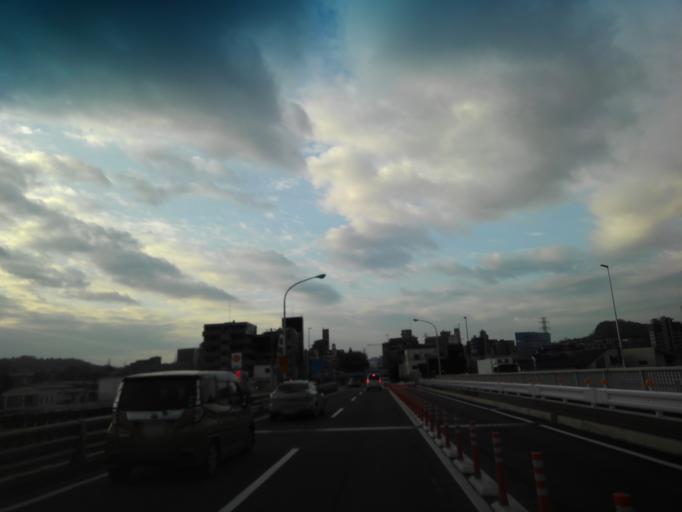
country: JP
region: Tokyo
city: Kokubunji
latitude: 35.6527
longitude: 139.4550
